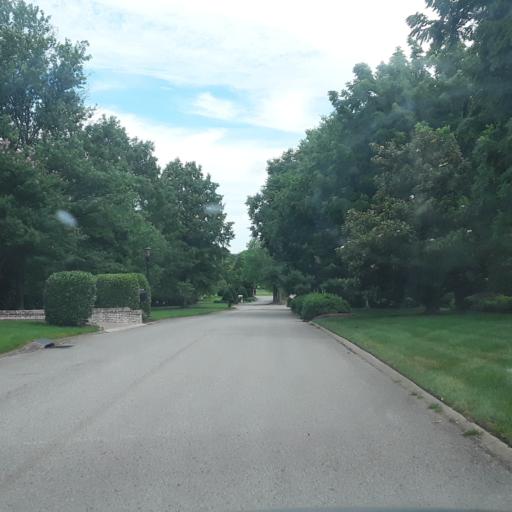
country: US
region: Tennessee
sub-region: Davidson County
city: Oak Hill
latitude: 36.0755
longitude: -86.7792
